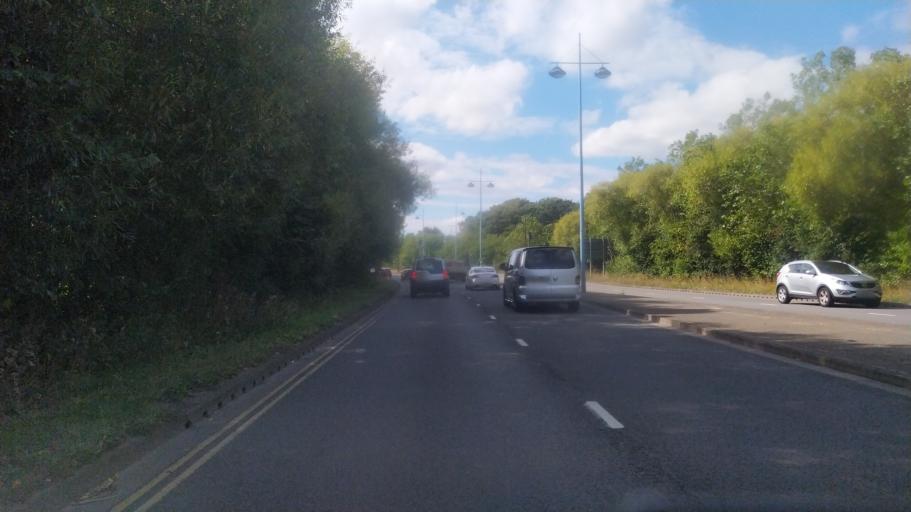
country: GB
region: England
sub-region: Southampton
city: Southampton
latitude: 50.9060
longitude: -1.4178
